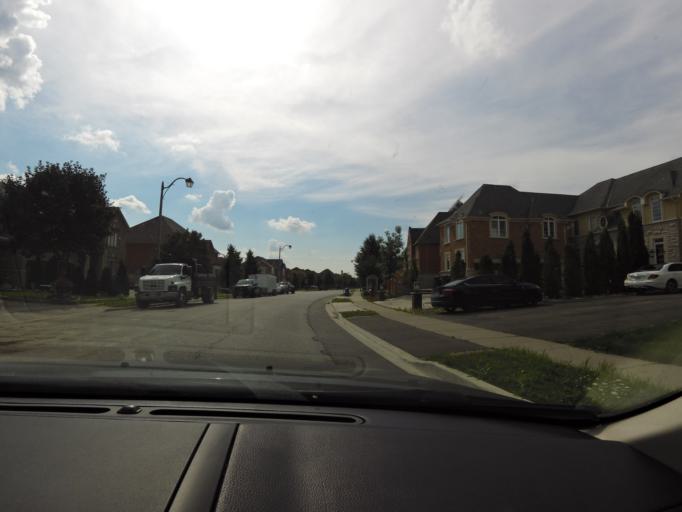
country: CA
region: Ontario
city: Brampton
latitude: 43.7944
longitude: -79.7526
